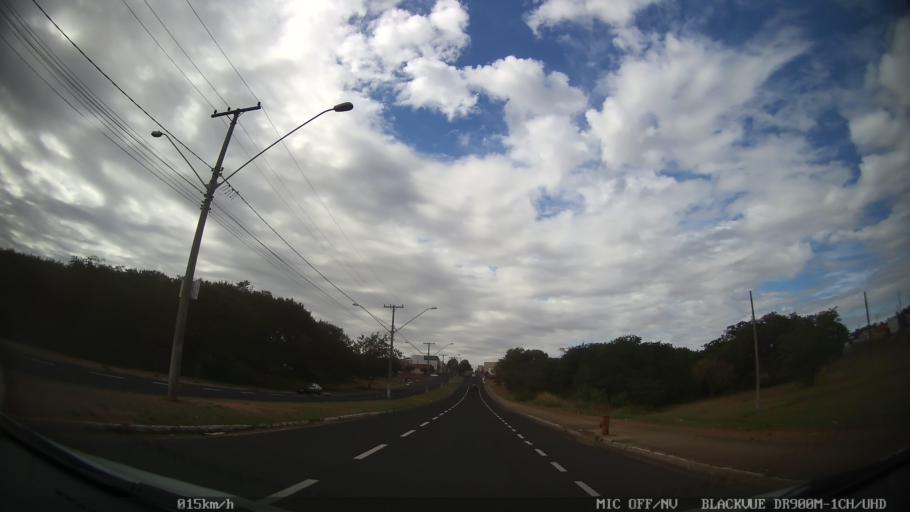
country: BR
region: Sao Paulo
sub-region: Sao Jose Do Rio Preto
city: Sao Jose do Rio Preto
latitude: -20.8030
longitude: -49.5038
